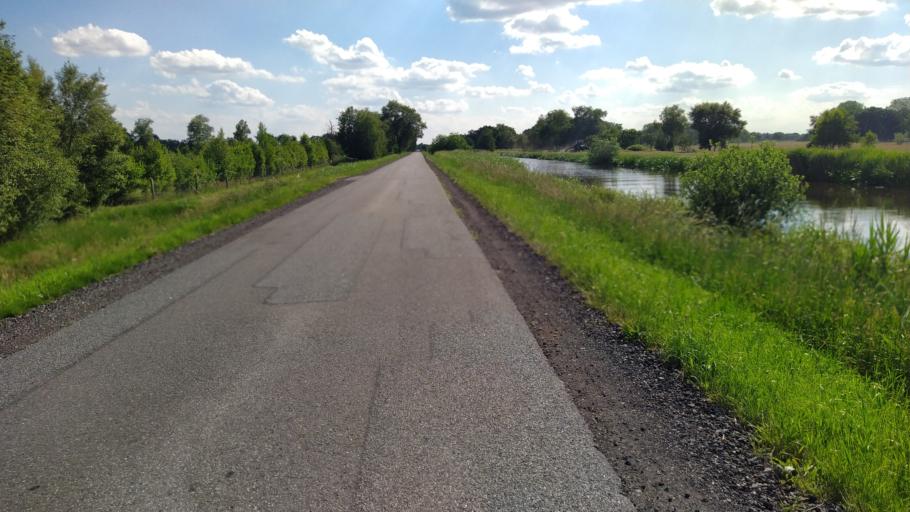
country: DE
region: Lower Saxony
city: Steinau
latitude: 53.6648
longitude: 8.9076
